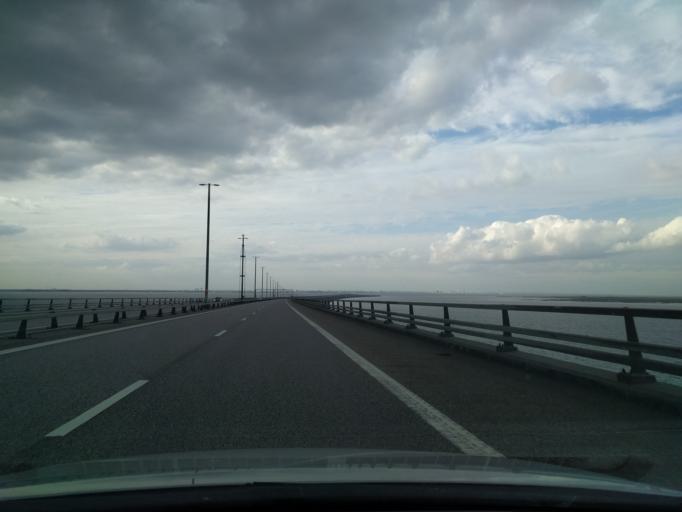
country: DK
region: Capital Region
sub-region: Dragor Kommune
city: Dragor
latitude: 55.5840
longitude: 12.7937
